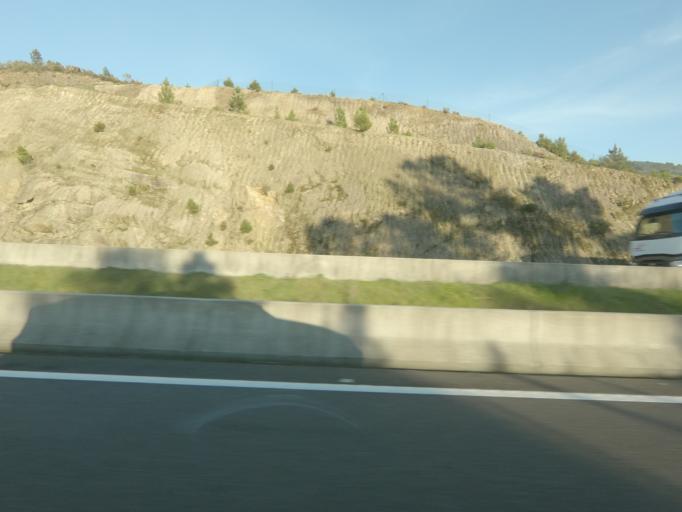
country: ES
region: Galicia
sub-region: Provincia de Ourense
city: Punxin
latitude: 42.3630
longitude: -7.9969
